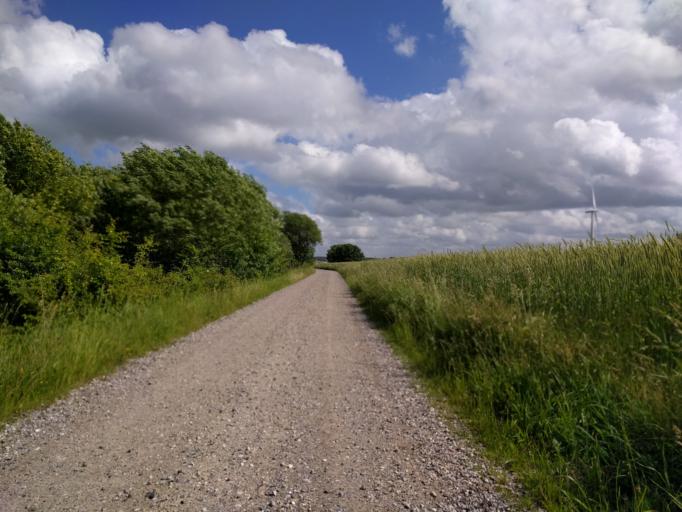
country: DK
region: South Denmark
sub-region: Kerteminde Kommune
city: Munkebo
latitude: 55.4646
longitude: 10.5155
